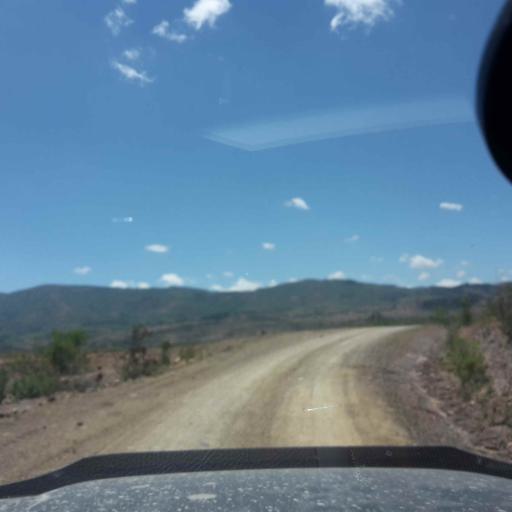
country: BO
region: Cochabamba
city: Totora
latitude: -17.7725
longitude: -65.2678
